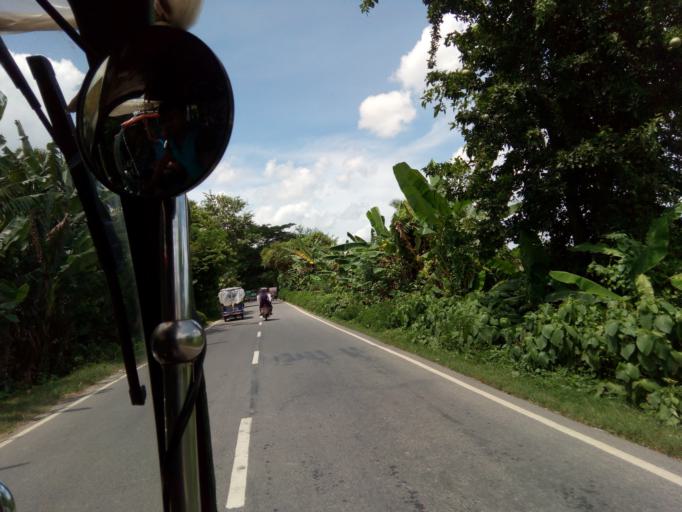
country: BD
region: Dhaka
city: Tungipara
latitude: 22.9577
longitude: 89.8196
